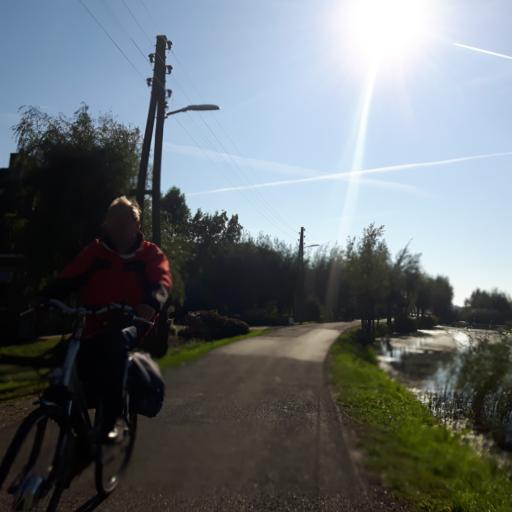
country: NL
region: South Holland
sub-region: Gemeente Schoonhoven
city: Schoonhoven
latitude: 51.9636
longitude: 4.8431
